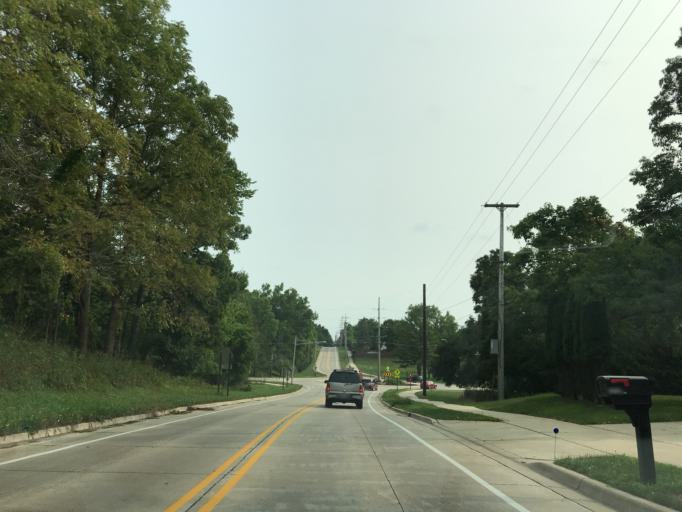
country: US
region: Michigan
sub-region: Ingham County
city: Okemos
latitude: 42.7420
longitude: -84.4475
